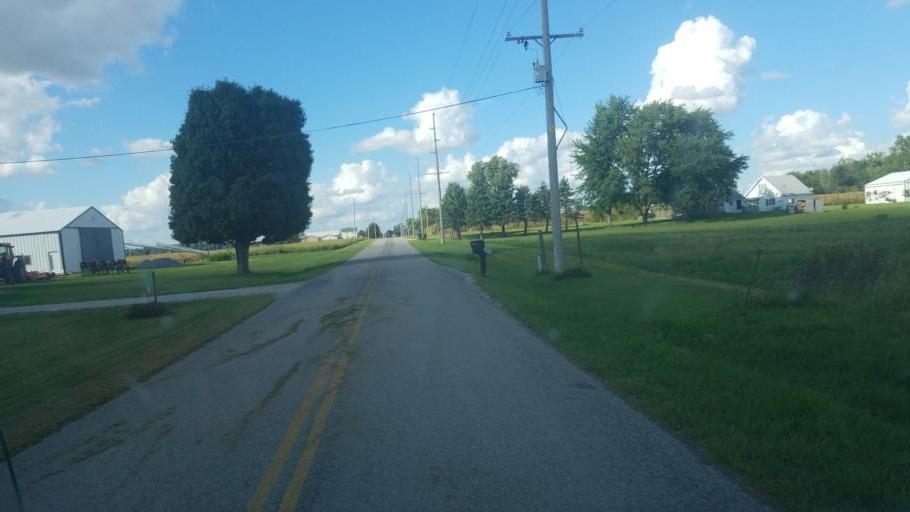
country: US
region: Ohio
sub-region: Hardin County
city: Kenton
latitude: 40.6973
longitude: -83.6921
